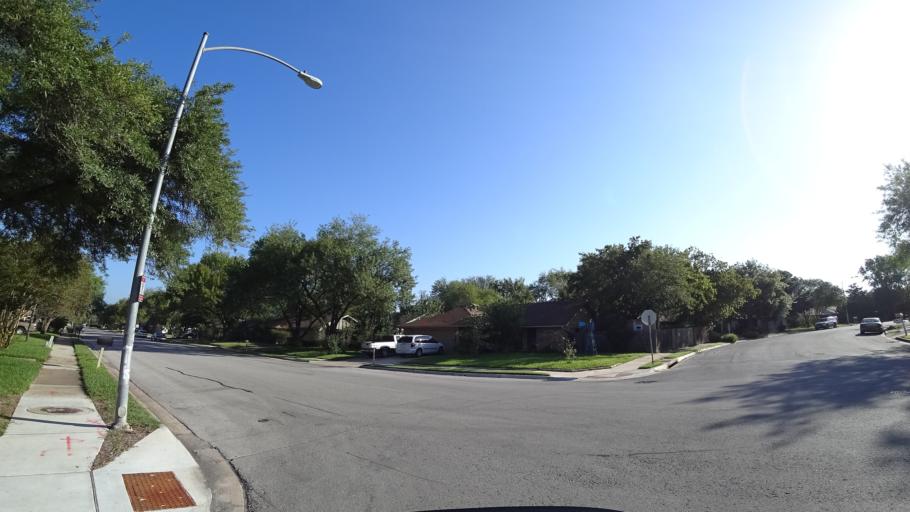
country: US
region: Texas
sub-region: Travis County
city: Shady Hollow
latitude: 30.2109
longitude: -97.8129
